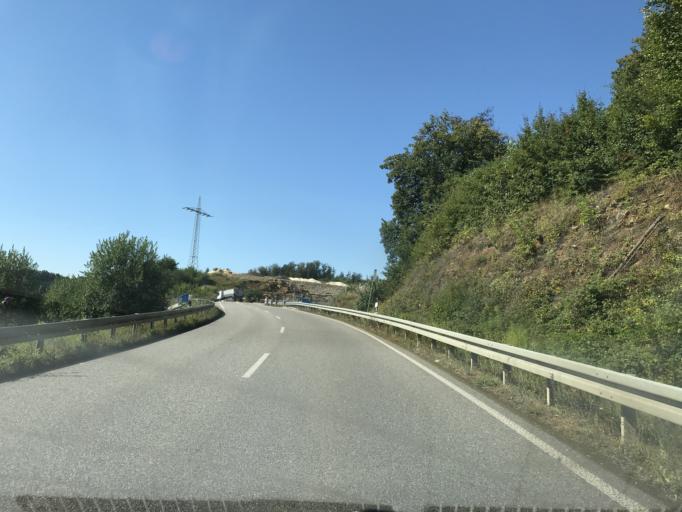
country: DE
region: Baden-Wuerttemberg
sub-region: Freiburg Region
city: Rheinfelden (Baden)
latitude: 47.5912
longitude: 7.7896
